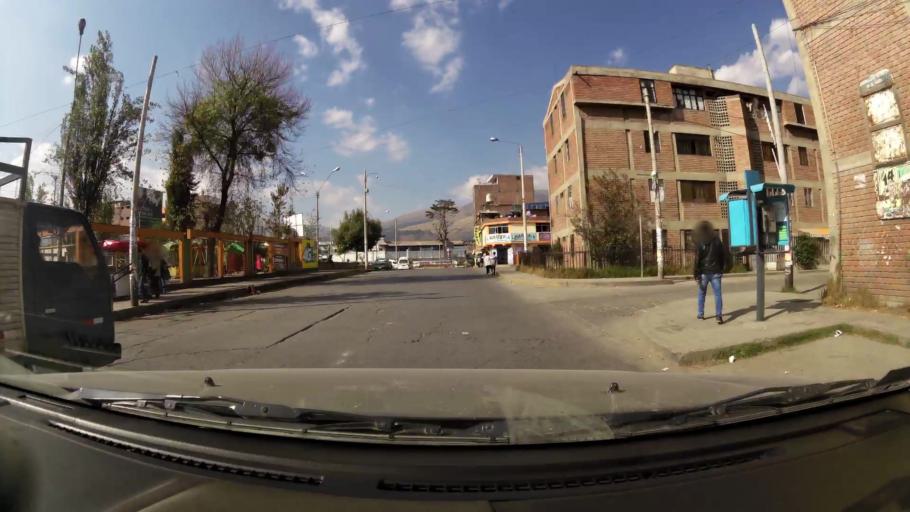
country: PE
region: Junin
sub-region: Provincia de Huancayo
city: El Tambo
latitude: -12.0600
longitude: -75.2117
